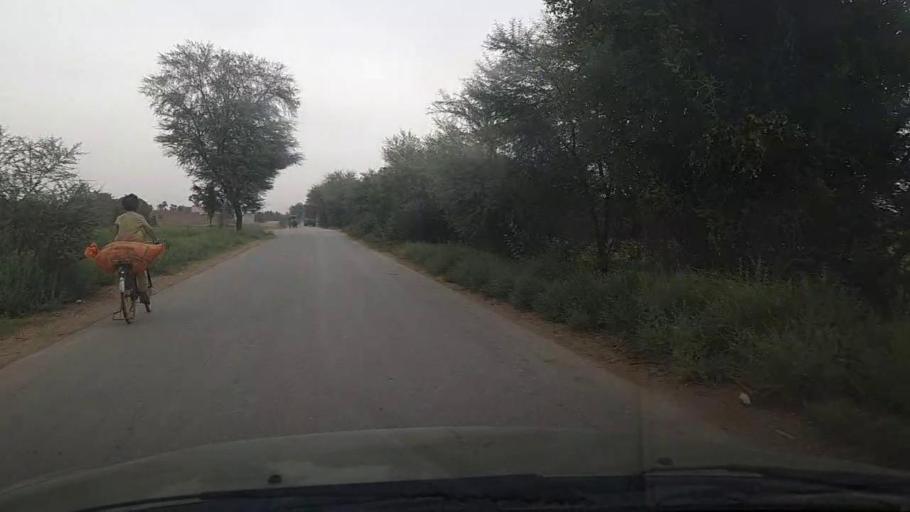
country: PK
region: Sindh
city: Daulatpur
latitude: 26.3190
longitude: 68.1040
